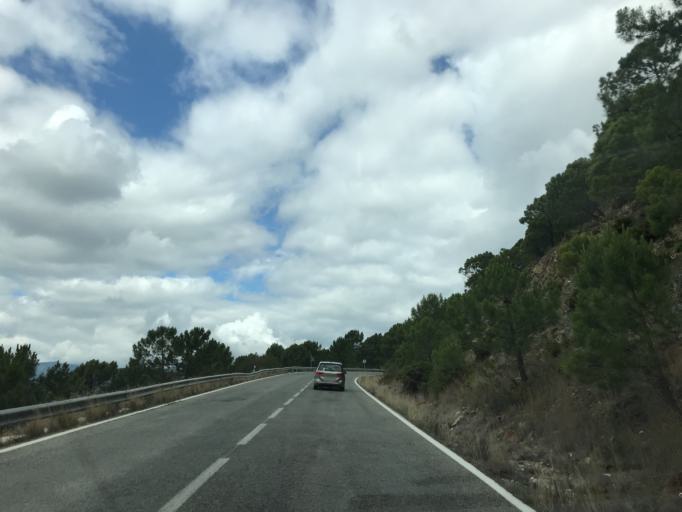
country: ES
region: Andalusia
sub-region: Provincia de Malaga
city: Benahavis
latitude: 36.5598
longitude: -5.0535
